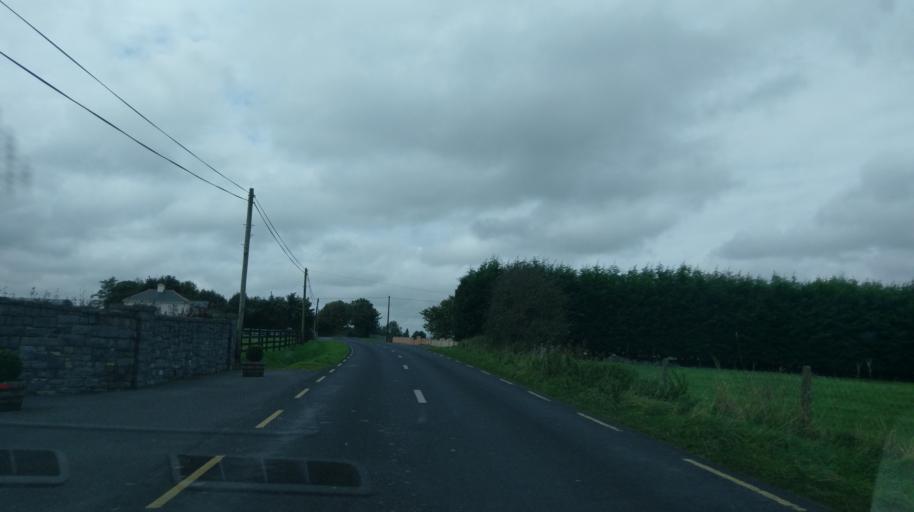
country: IE
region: Connaught
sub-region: County Galway
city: Ballinasloe
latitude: 53.3946
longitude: -8.3463
